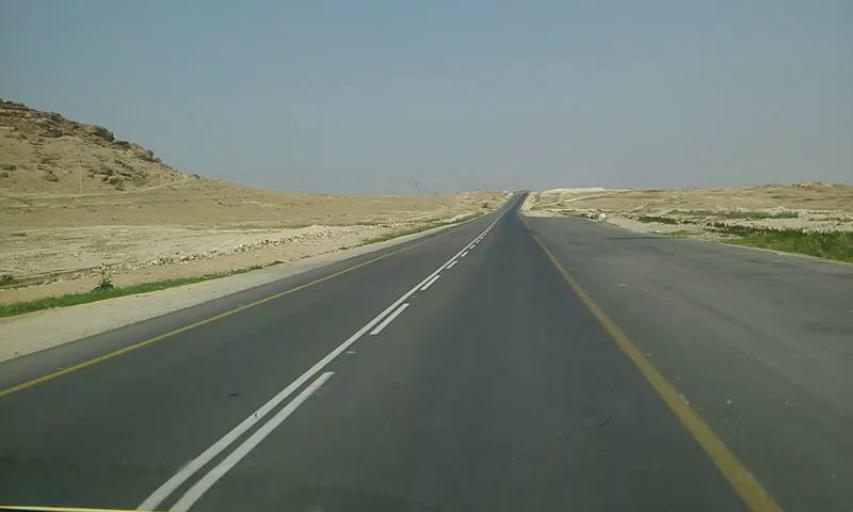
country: PS
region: West Bank
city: Al `Awja
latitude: 31.9673
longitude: 35.4703
